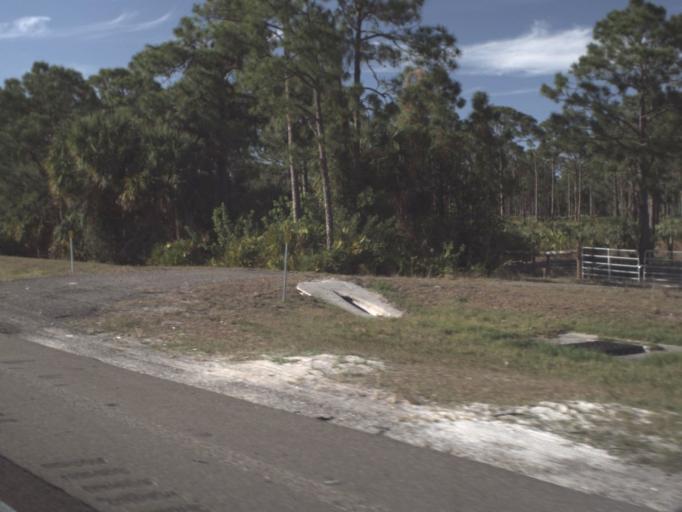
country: US
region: Florida
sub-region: Indian River County
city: Roseland
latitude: 27.8299
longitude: -80.5615
